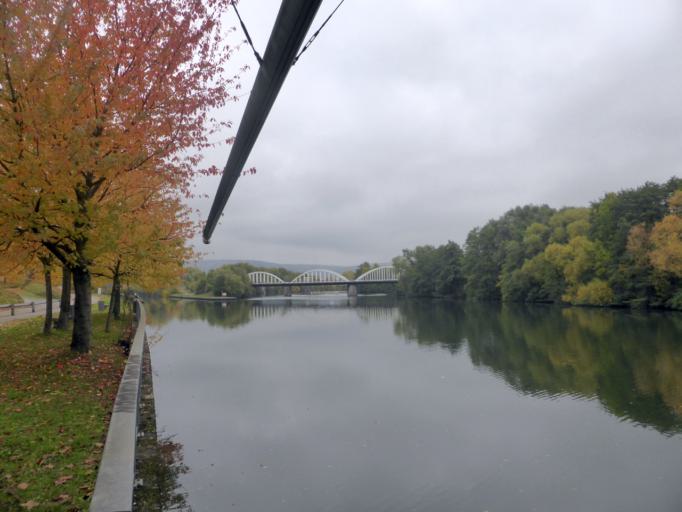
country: FR
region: Lorraine
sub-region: Departement de Meurthe-et-Moselle
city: Frouard
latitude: 48.7757
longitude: 6.1356
